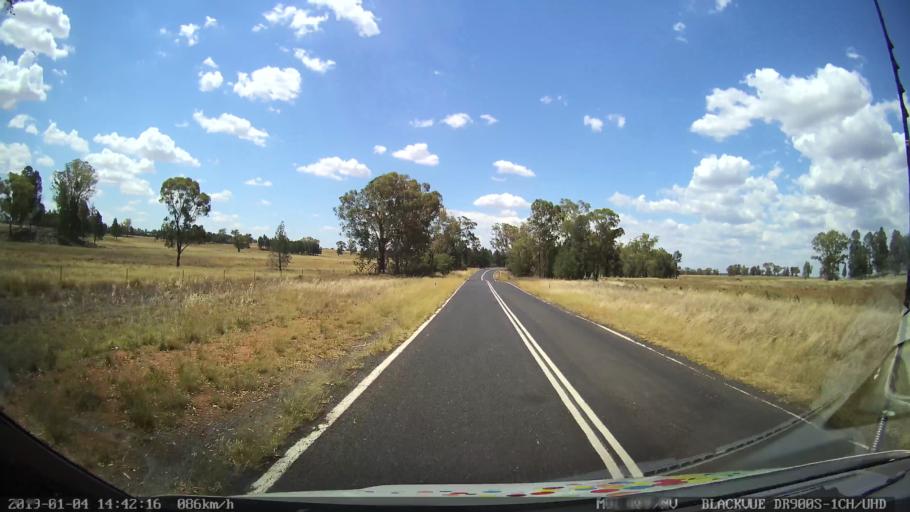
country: AU
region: New South Wales
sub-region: Dubbo Municipality
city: Dubbo
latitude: -32.1301
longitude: 148.6410
